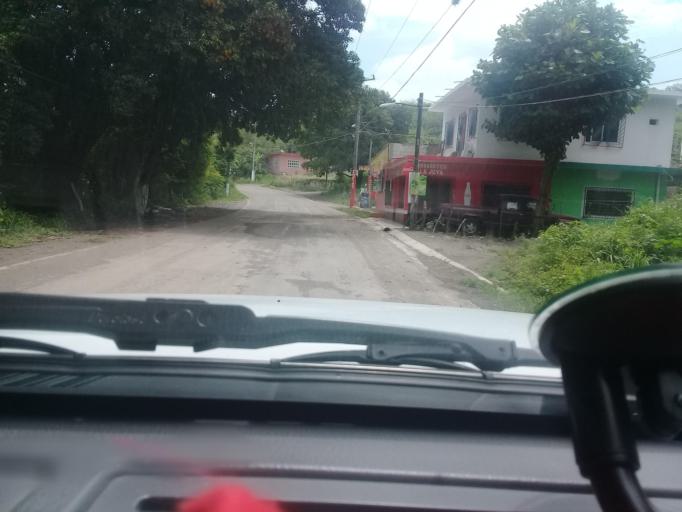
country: MX
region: Veracruz
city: Paso de Ovejas
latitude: 19.2822
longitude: -96.4313
